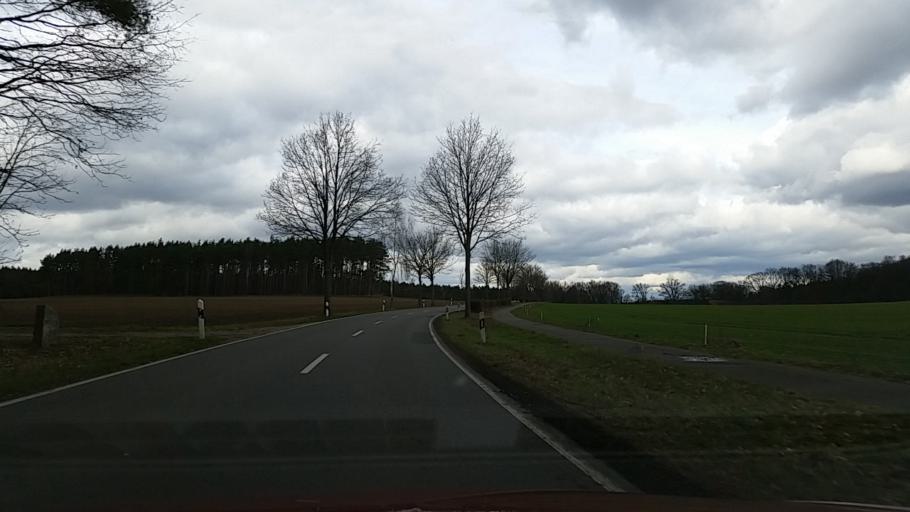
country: DE
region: Lower Saxony
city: Zernien
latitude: 53.0929
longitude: 10.9451
